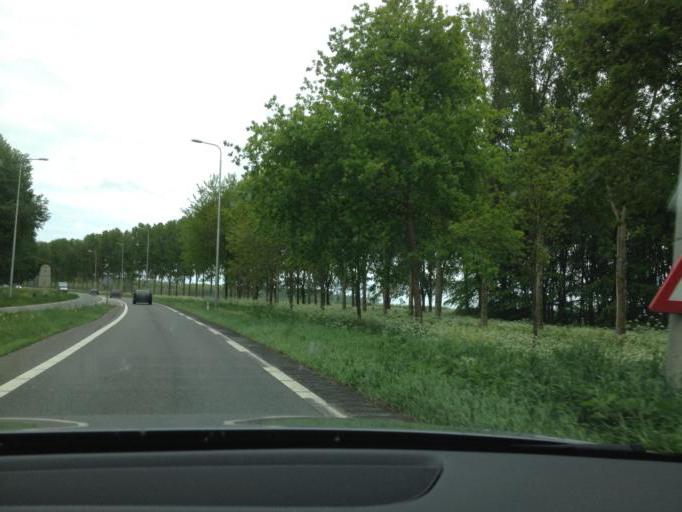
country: NL
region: North Holland
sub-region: Gemeente Huizen
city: Huizen
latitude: 52.3366
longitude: 5.2698
